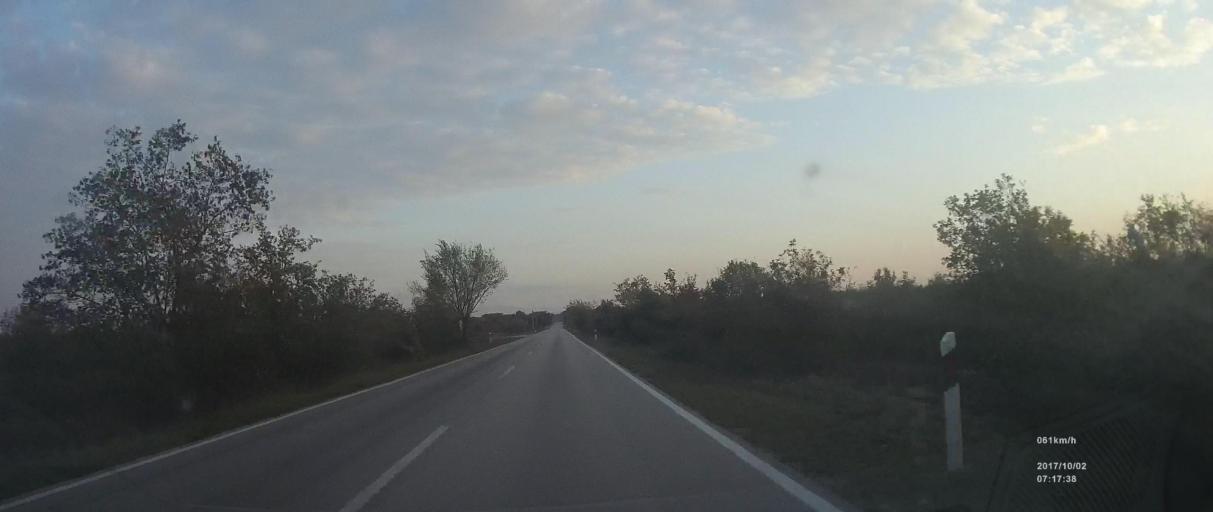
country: HR
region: Zadarska
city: Benkovac
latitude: 44.0114
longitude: 15.5926
